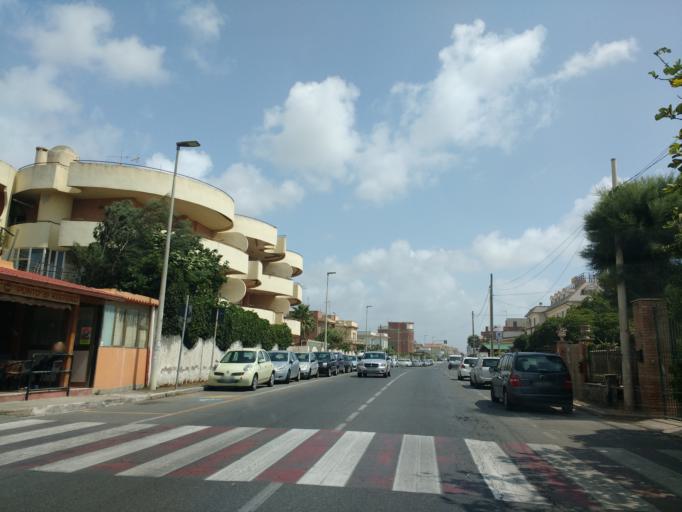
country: IT
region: Latium
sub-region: Citta metropolitana di Roma Capitale
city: Torvaianica
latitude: 41.6446
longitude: 12.4338
